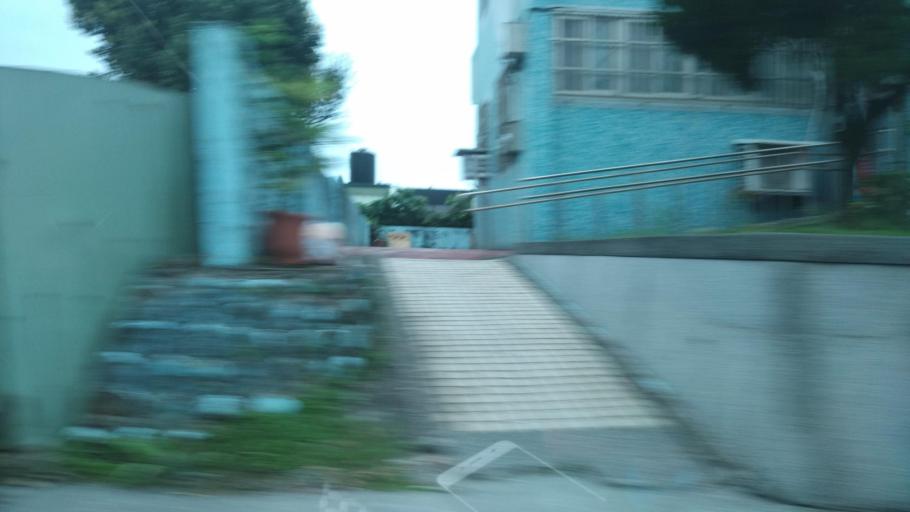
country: TW
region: Taiwan
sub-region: Keelung
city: Keelung
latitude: 25.2124
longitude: 121.6466
